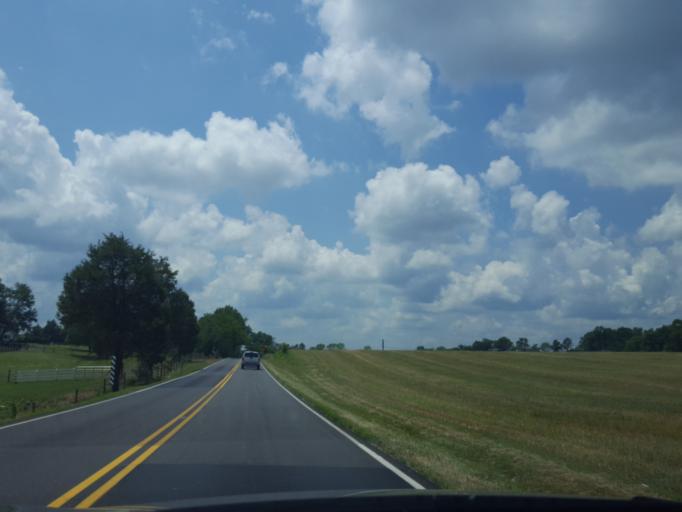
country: US
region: Virginia
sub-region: Orange County
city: Gordonsville
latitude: 38.1269
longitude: -78.2165
